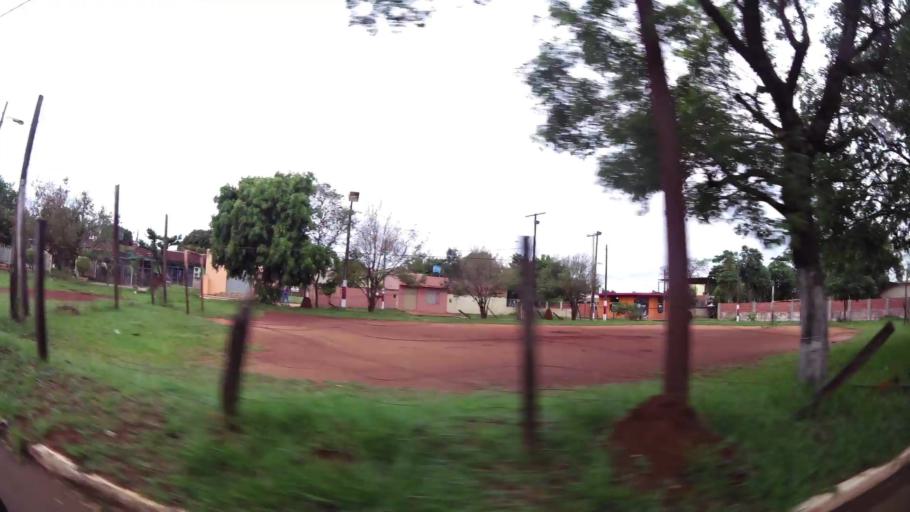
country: PY
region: Alto Parana
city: Ciudad del Este
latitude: -25.4070
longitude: -54.6290
